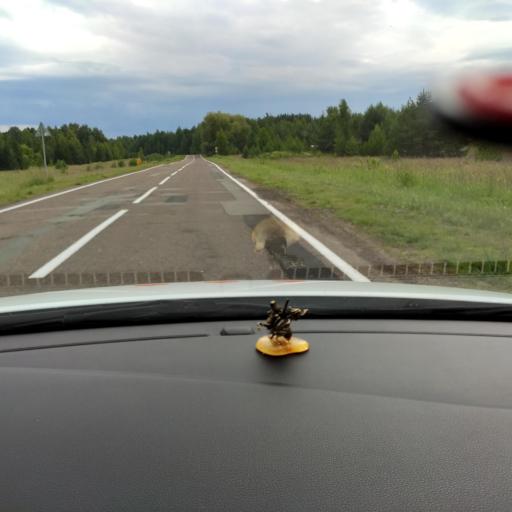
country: RU
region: Tatarstan
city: Kuybyshevskiy Zaton
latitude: 55.3637
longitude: 49.2897
